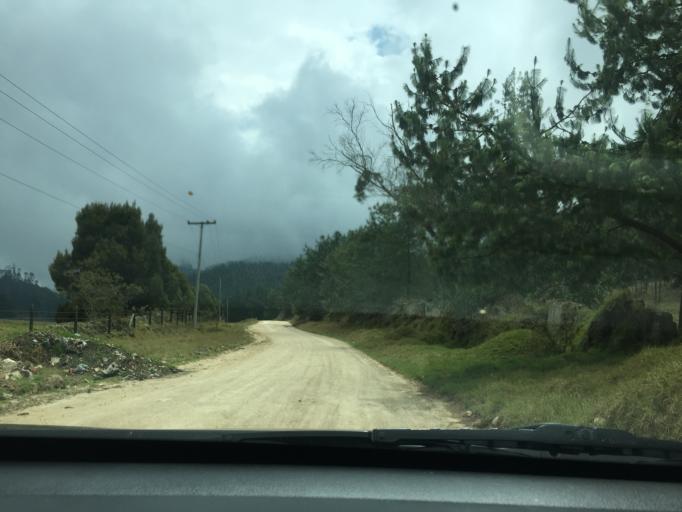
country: CO
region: Cundinamarca
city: Bojaca
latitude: 4.6913
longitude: -74.3169
